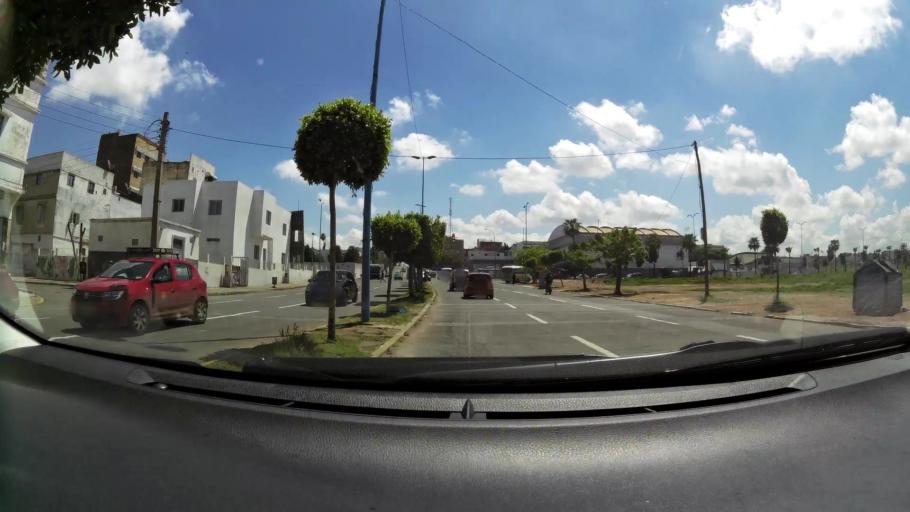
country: MA
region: Grand Casablanca
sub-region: Casablanca
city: Casablanca
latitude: 33.5606
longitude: -7.5759
